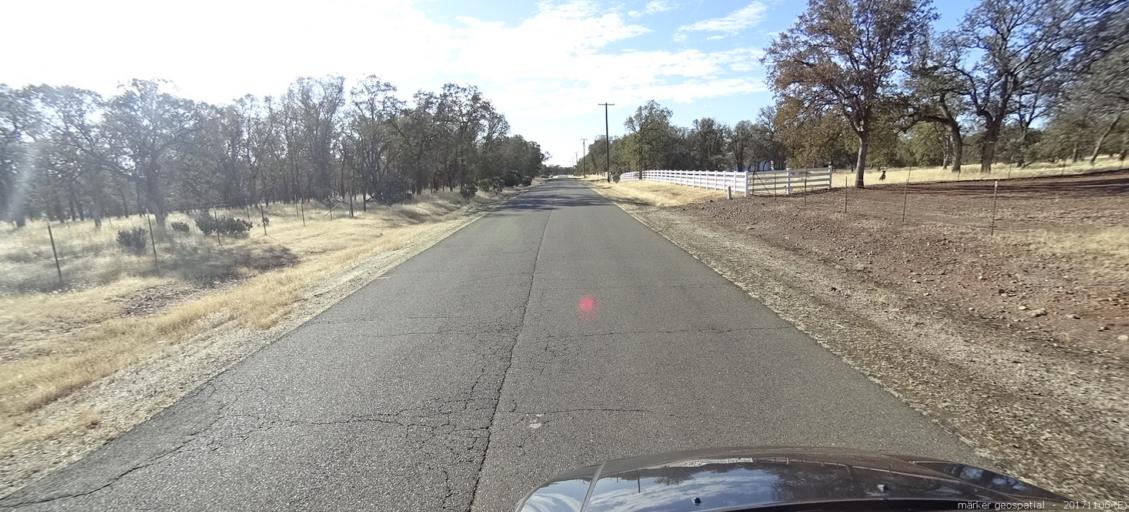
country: US
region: California
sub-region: Shasta County
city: Palo Cedro
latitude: 40.5152
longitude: -122.2482
